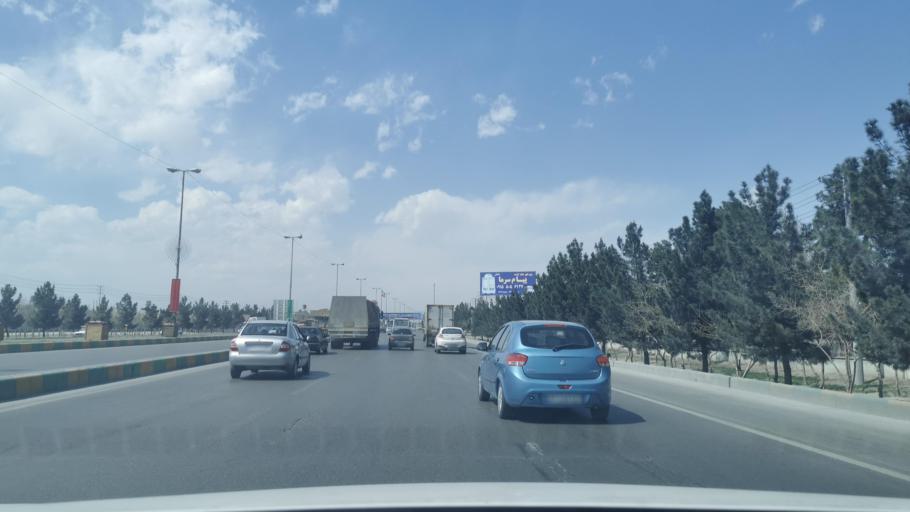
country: IR
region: Razavi Khorasan
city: Torqabeh
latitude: 36.4195
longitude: 59.4639
